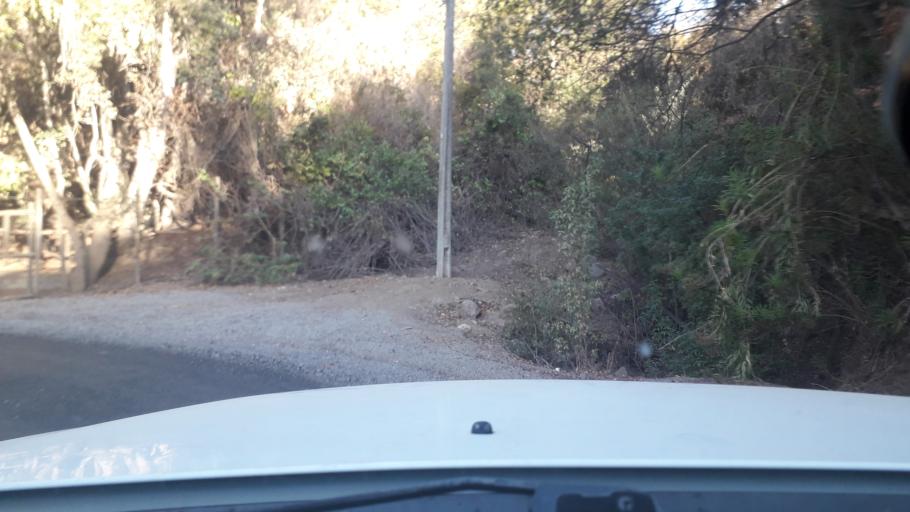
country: CL
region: Valparaiso
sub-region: Provincia de Marga Marga
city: Limache
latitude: -33.0469
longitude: -71.0582
